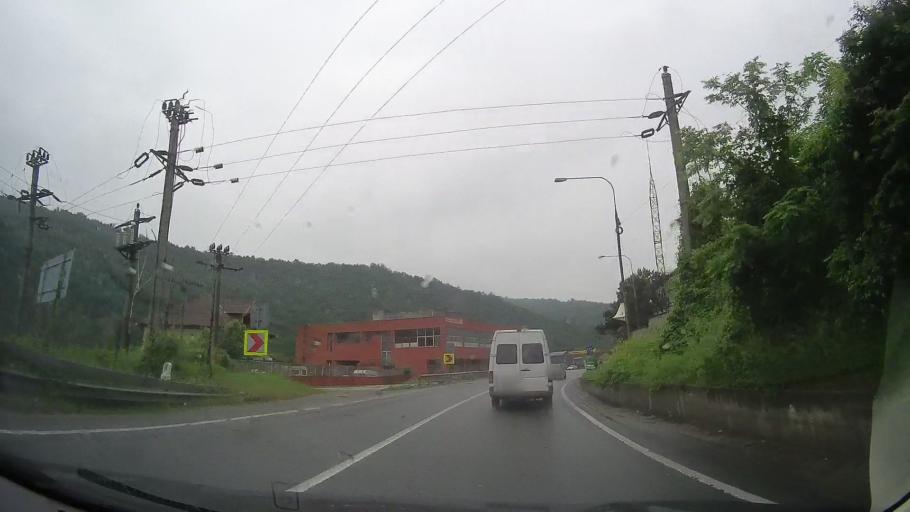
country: RO
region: Mehedinti
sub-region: Municipiul Orsova
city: Orsova
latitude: 44.7417
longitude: 22.4097
